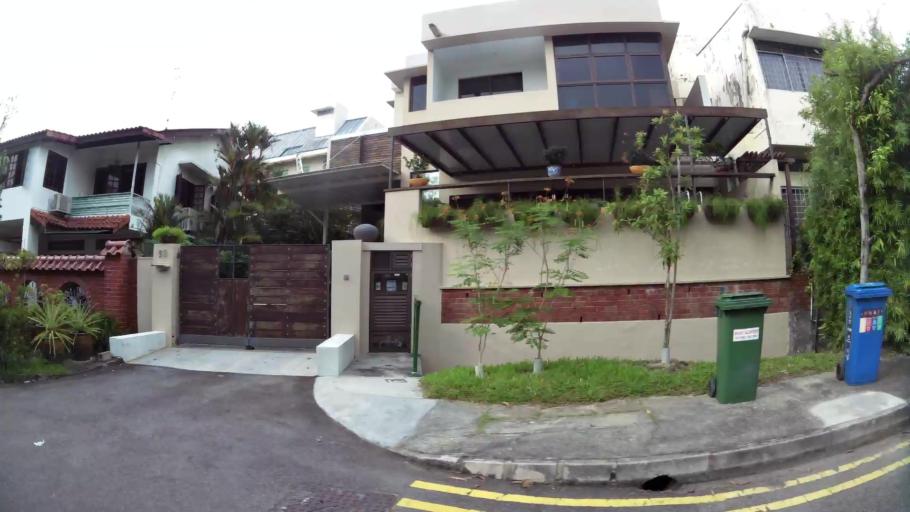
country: SG
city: Singapore
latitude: 1.3506
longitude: 103.8456
